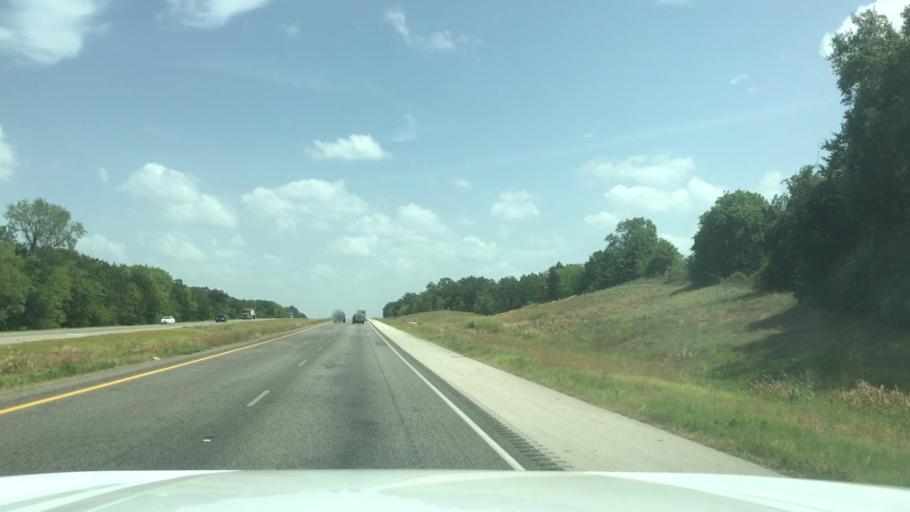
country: US
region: Texas
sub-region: Robertson County
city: Calvert
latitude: 30.9418
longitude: -96.6435
